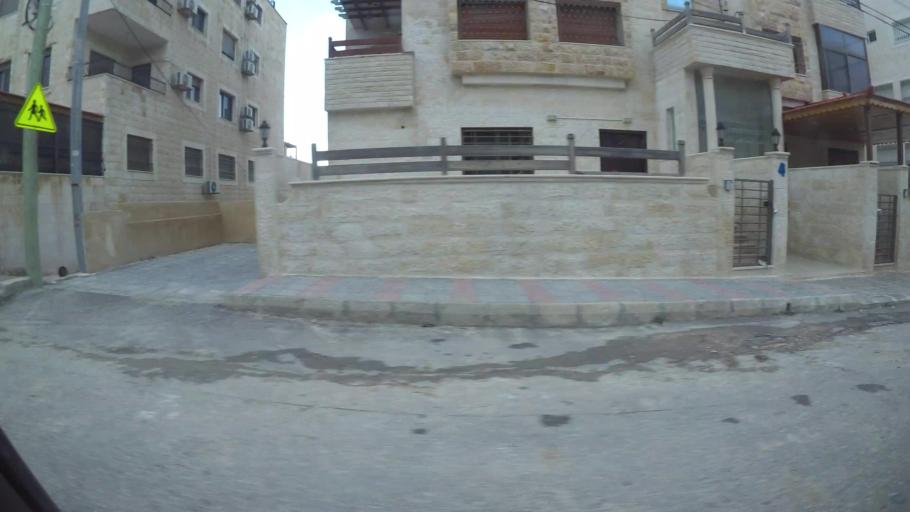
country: JO
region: Amman
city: Al Jubayhah
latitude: 32.0482
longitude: 35.8970
